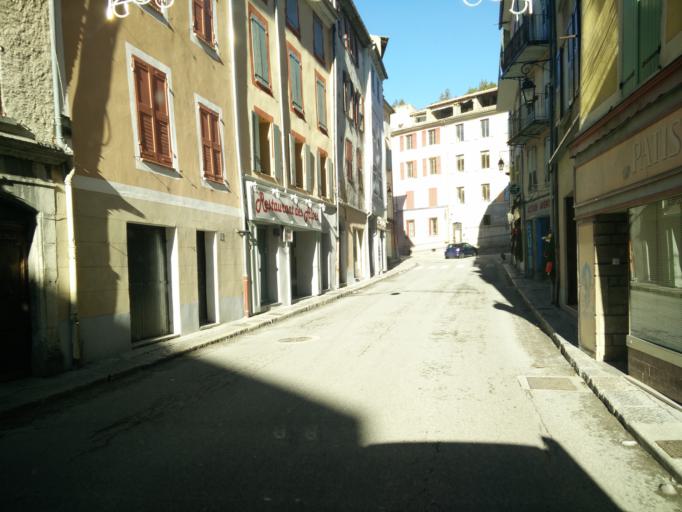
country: FR
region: Provence-Alpes-Cote d'Azur
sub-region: Departement des Alpes-de-Haute-Provence
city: Castellane
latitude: 43.8472
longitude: 6.5122
